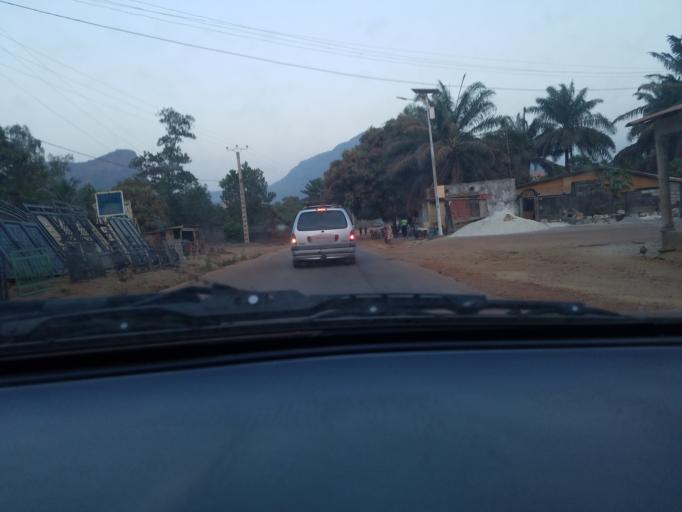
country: GN
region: Kindia
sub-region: Prefecture de Dubreka
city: Dubreka
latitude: 9.7890
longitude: -13.5022
